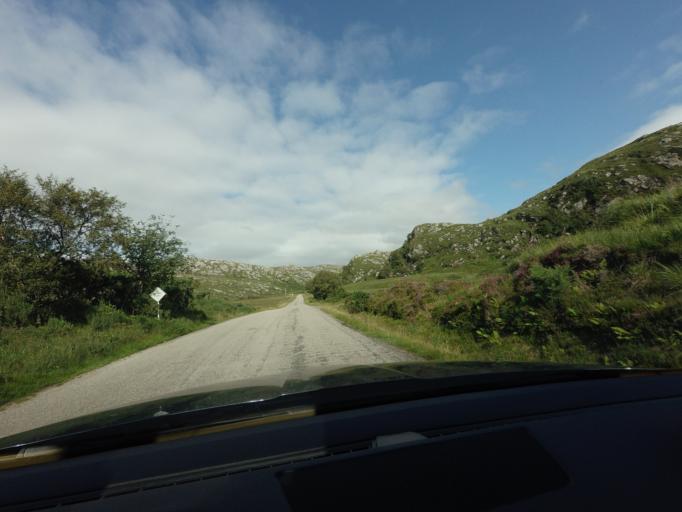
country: GB
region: Scotland
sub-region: Highland
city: Ullapool
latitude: 58.3747
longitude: -5.0126
